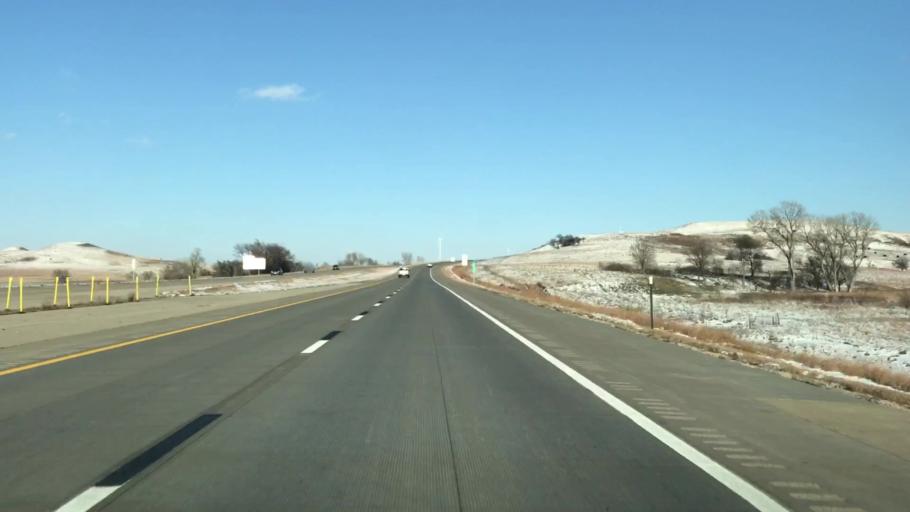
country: US
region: Kansas
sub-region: Ellsworth County
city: Ellsworth
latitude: 38.8627
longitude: -98.1013
